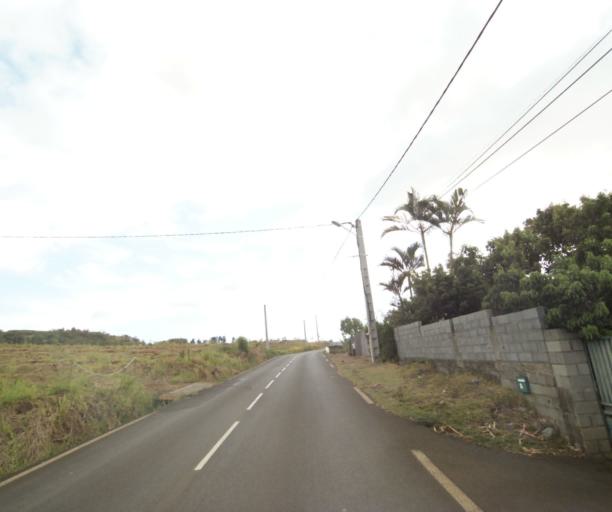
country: RE
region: Reunion
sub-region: Reunion
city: Trois-Bassins
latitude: -21.0617
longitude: 55.2806
